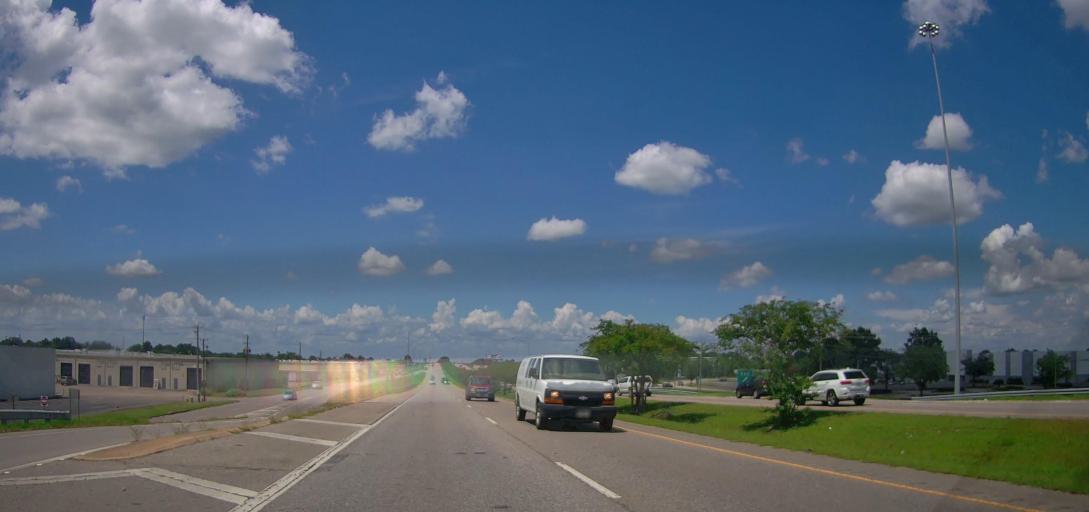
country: US
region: Alabama
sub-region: Montgomery County
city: Montgomery
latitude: 32.3837
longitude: -86.2104
